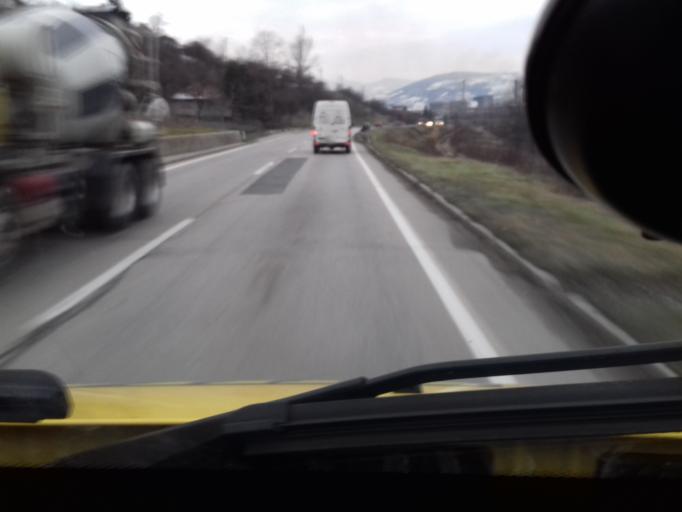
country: BA
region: Federation of Bosnia and Herzegovina
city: Zenica
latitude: 44.2450
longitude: 17.8999
